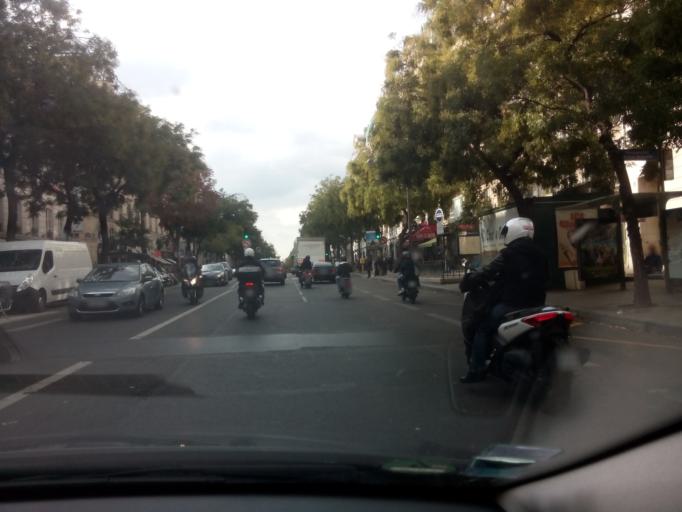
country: FR
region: Ile-de-France
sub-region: Paris
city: Paris
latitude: 48.8707
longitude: 2.3475
